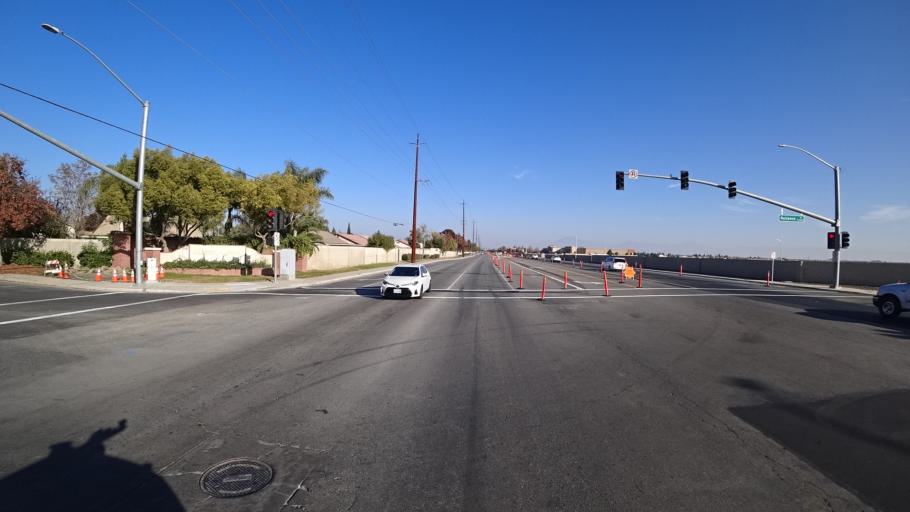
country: US
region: California
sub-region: Kern County
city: Greenfield
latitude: 35.2961
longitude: -119.0832
